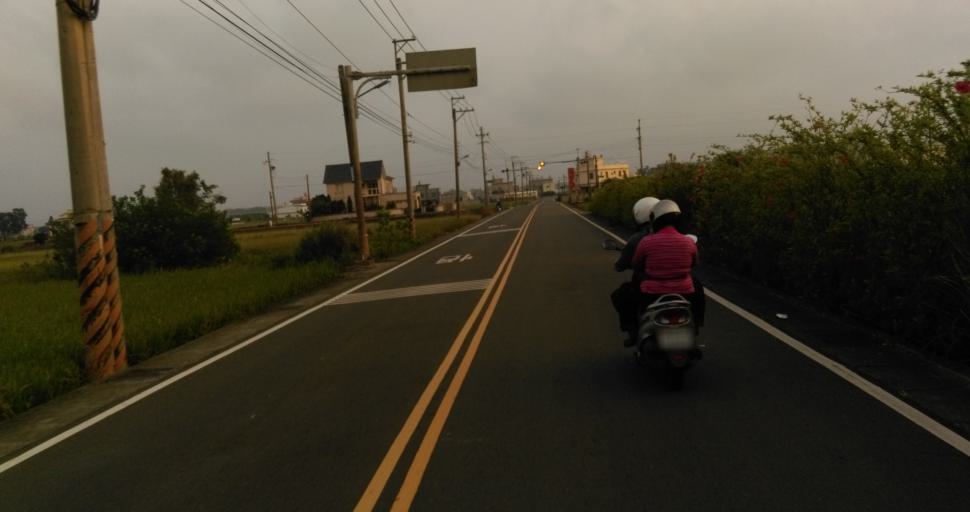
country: TW
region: Taiwan
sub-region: Hsinchu
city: Zhubei
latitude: 24.8733
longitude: 120.9565
